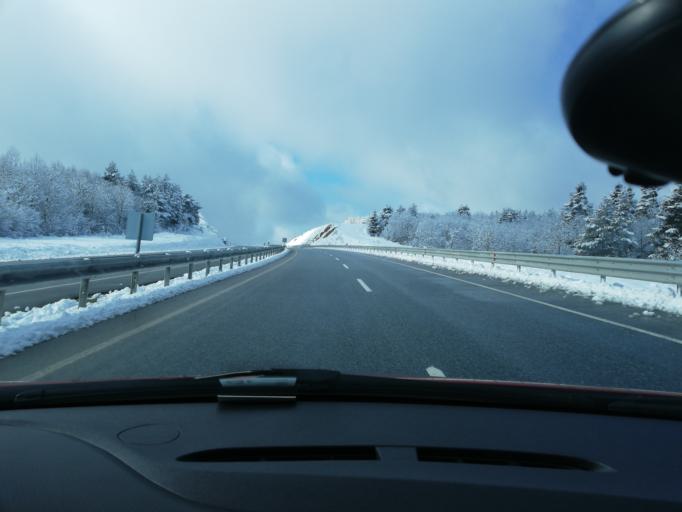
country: TR
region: Kastamonu
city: Kuzyaka
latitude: 41.3351
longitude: 33.6255
